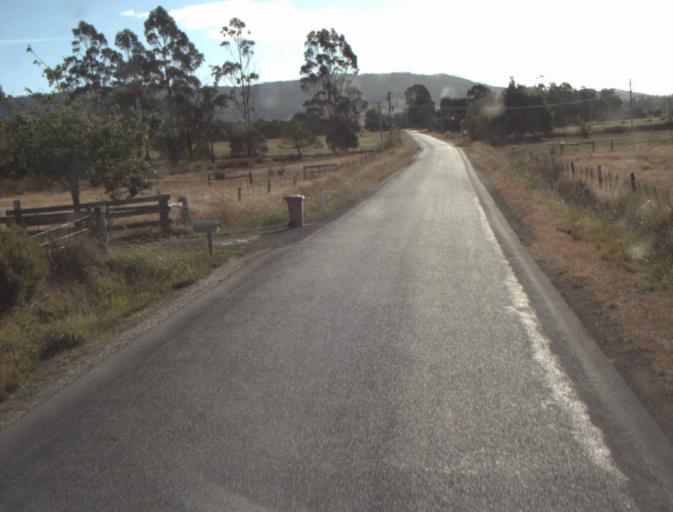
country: AU
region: Tasmania
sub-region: Launceston
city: Mayfield
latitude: -41.2393
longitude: 147.1684
